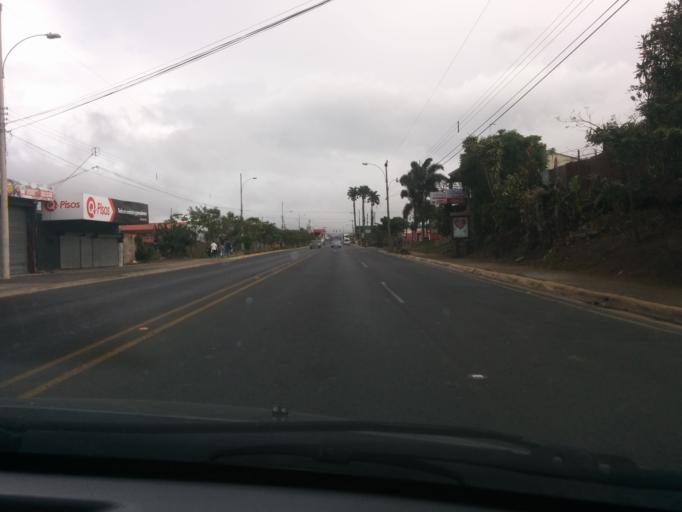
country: CR
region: Alajuela
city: San Ramon
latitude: 10.0795
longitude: -84.4698
